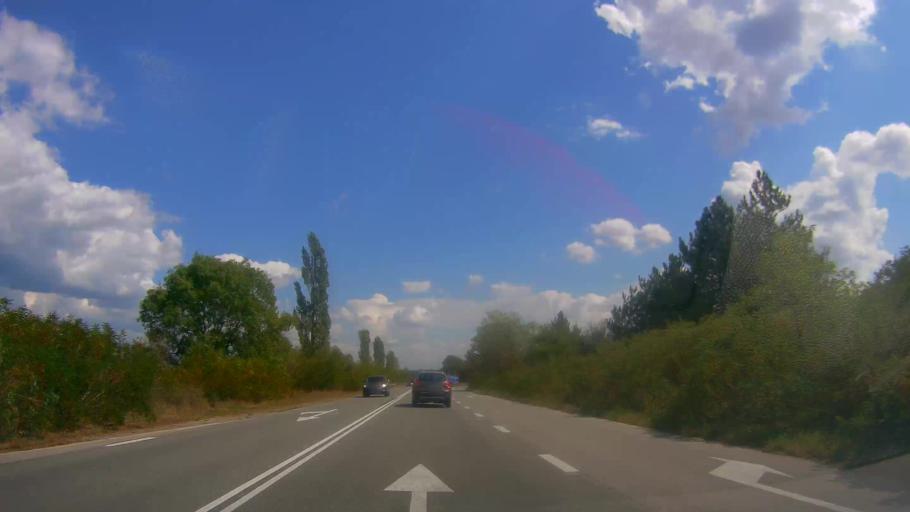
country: BG
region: Sliven
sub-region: Obshtina Tvurditsa
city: Tvurditsa
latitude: 42.6517
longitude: 25.9738
